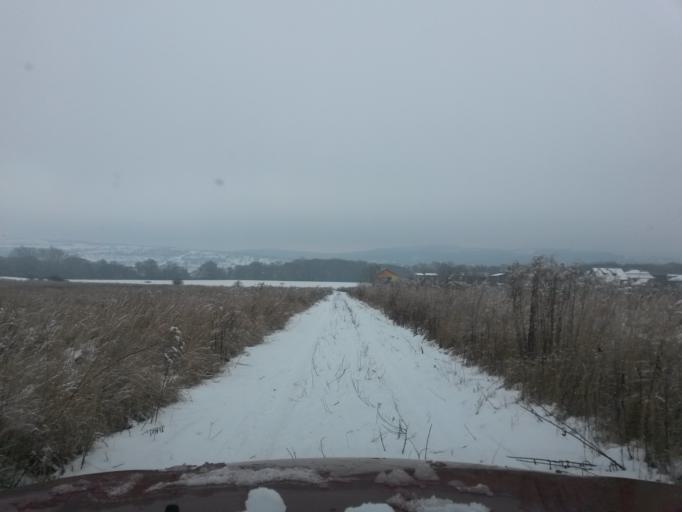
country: SK
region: Kosicky
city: Kosice
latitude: 48.7121
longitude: 21.3262
